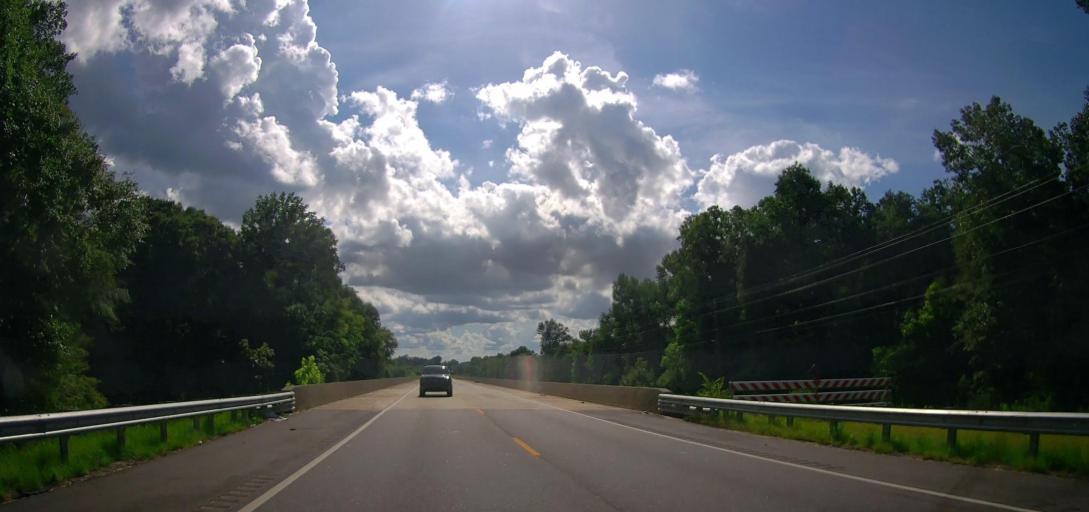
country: US
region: Alabama
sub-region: Russell County
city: Ladonia
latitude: 32.4619
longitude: -85.1308
